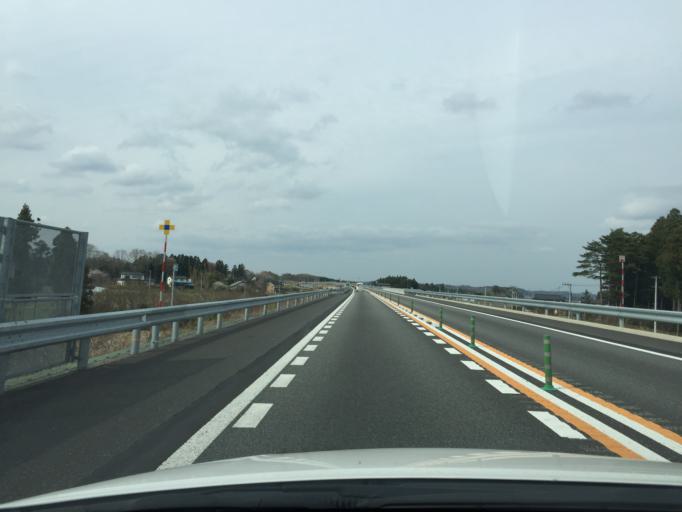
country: JP
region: Fukushima
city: Namie
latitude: 37.6128
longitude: 140.9267
